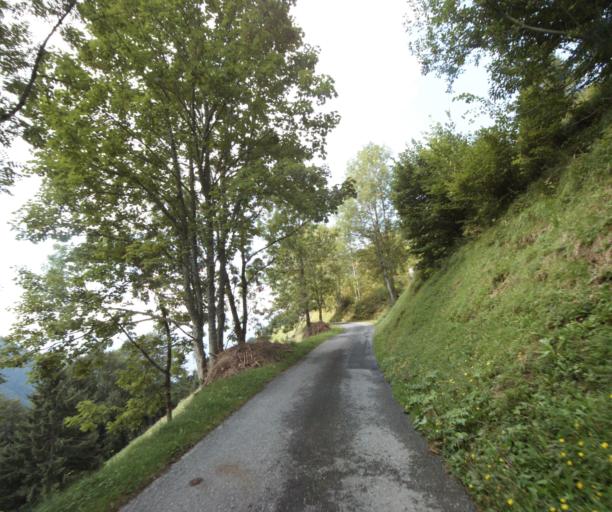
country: CH
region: Vaud
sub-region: Riviera-Pays-d'Enhaut District
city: Caux
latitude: 46.4201
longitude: 6.9741
